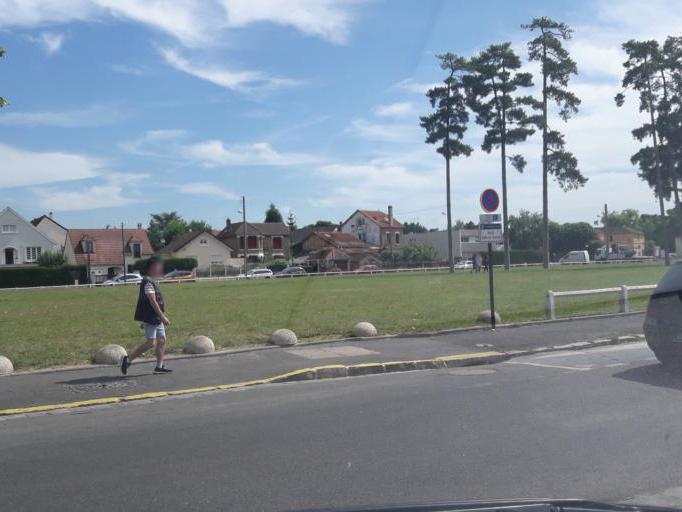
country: FR
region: Ile-de-France
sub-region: Departement de l'Essonne
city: Sainte-Genevieve-des-Bois
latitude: 48.6396
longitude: 2.3291
